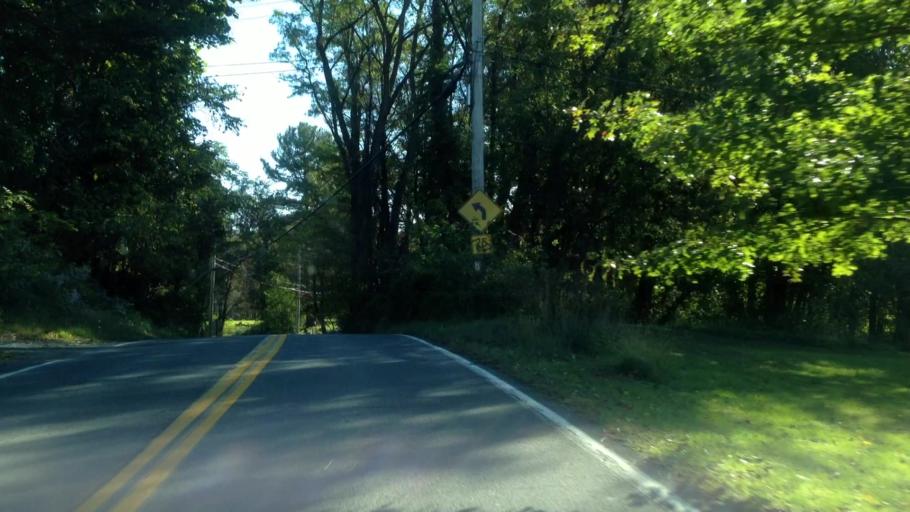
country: US
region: New York
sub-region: Ulster County
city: Port Ewen
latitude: 41.8528
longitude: -73.9885
